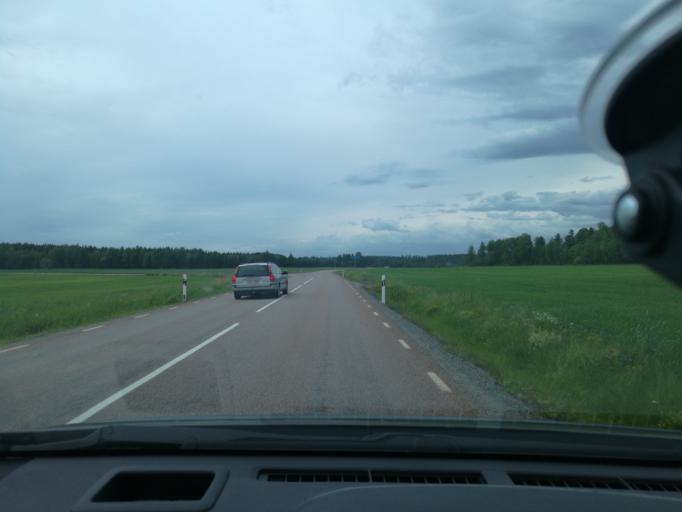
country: SE
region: Vaestmanland
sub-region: Vasteras
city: Skultuna
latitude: 59.7354
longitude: 16.4130
